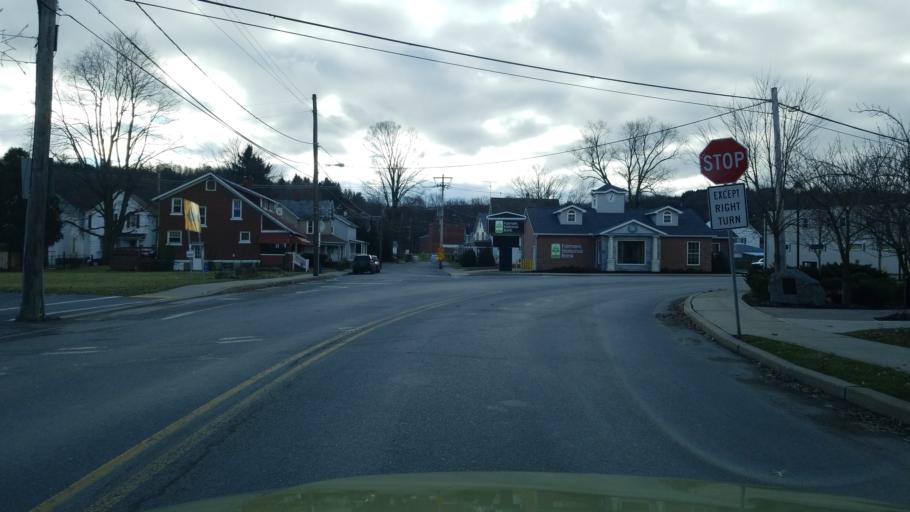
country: US
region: Pennsylvania
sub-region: Jefferson County
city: Punxsutawney
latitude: 40.9420
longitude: -78.9721
